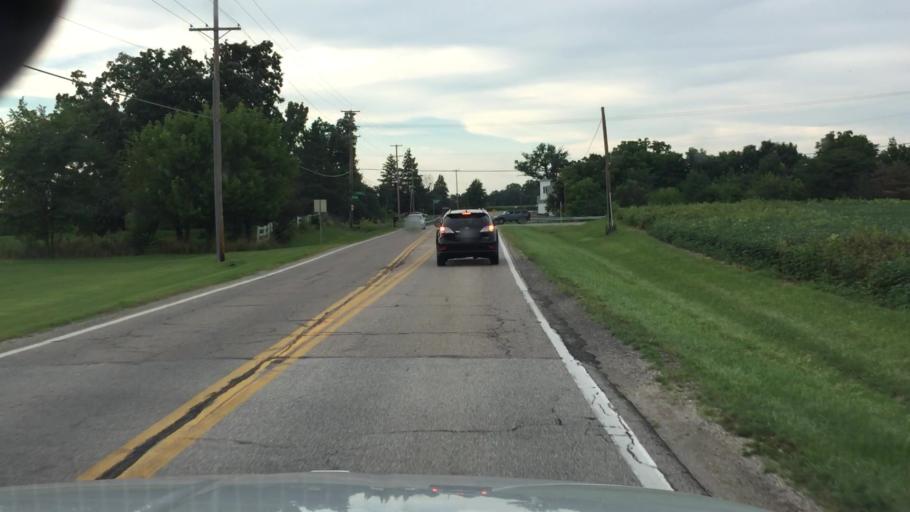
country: US
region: Ohio
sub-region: Madison County
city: Plain City
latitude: 40.0409
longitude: -83.2636
